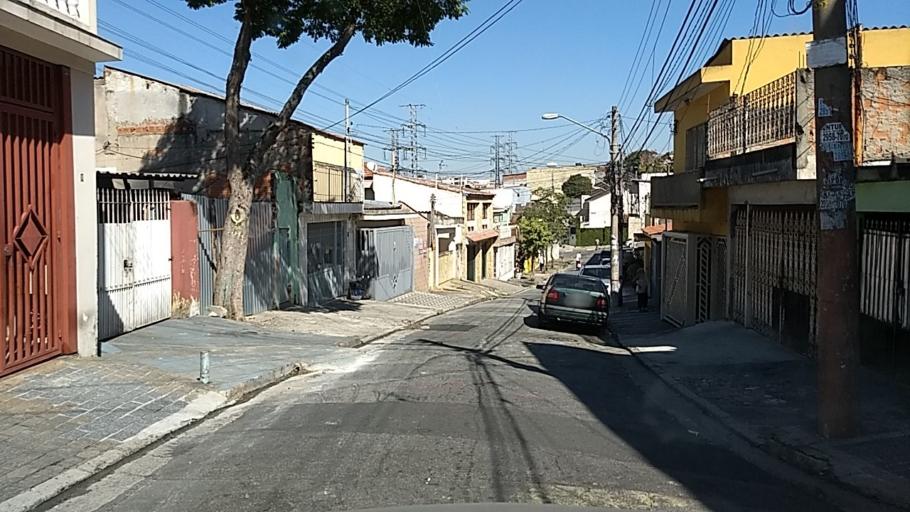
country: BR
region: Sao Paulo
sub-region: Guarulhos
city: Guarulhos
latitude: -23.4904
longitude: -46.5819
